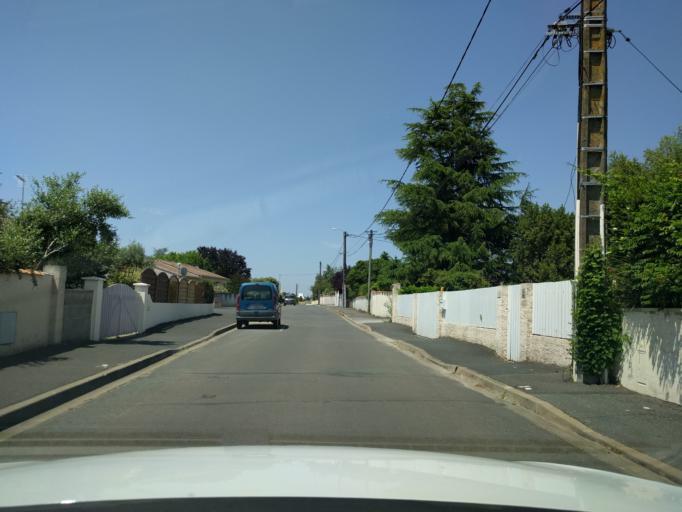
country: FR
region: Poitou-Charentes
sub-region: Departement des Deux-Sevres
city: Niort
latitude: 46.3522
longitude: -0.4735
